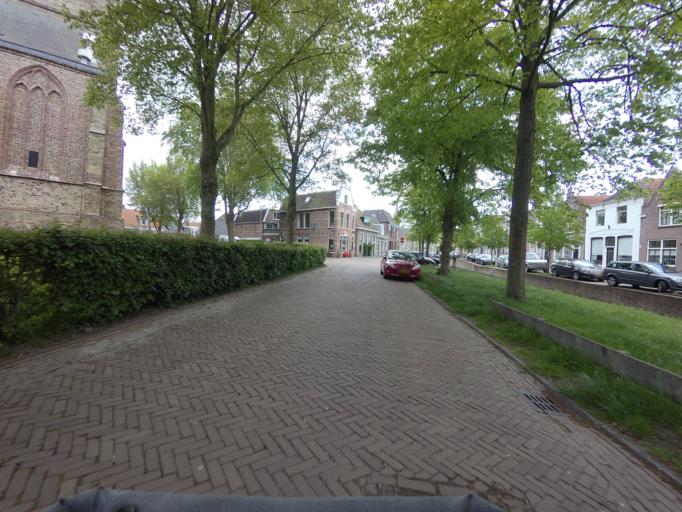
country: NL
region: Friesland
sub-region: Sudwest Fryslan
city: Bolsward
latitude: 53.0650
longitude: 5.5259
